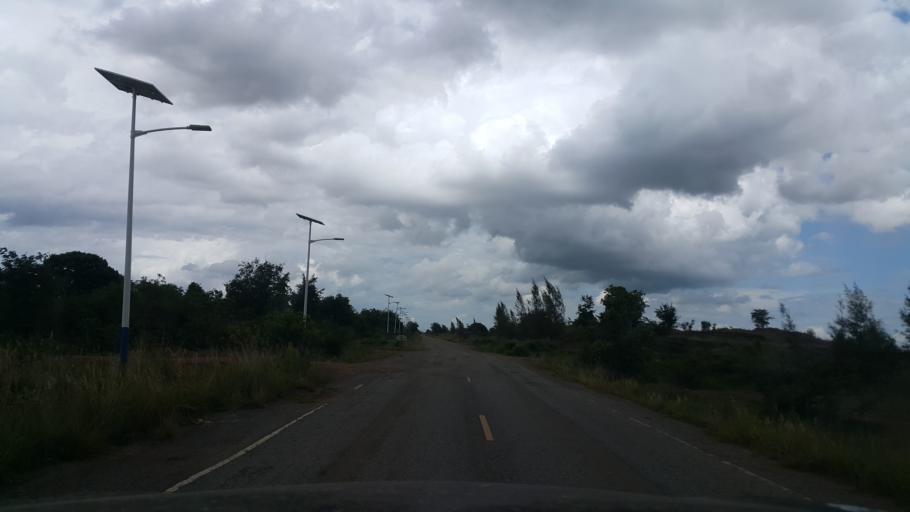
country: TH
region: Sukhothai
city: Ban Na
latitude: 17.0603
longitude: 99.7778
